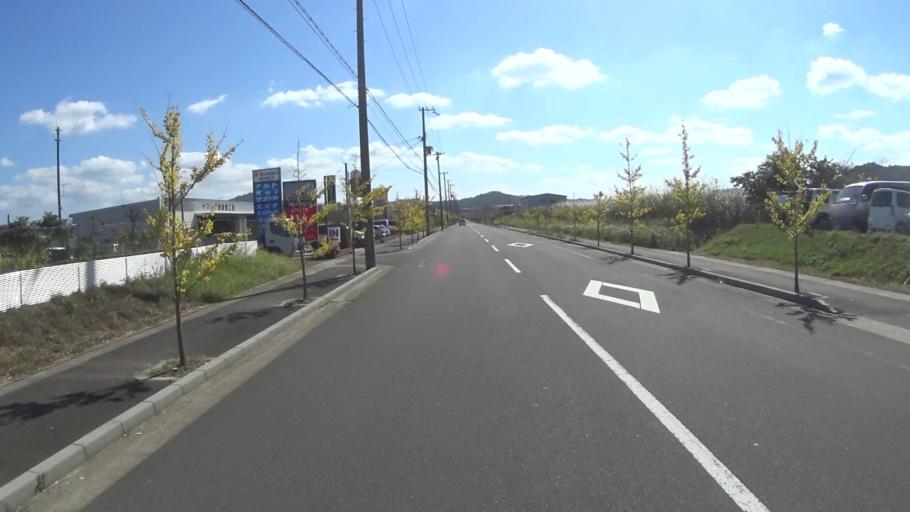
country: JP
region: Kyoto
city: Miyazu
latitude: 35.6829
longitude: 135.0193
